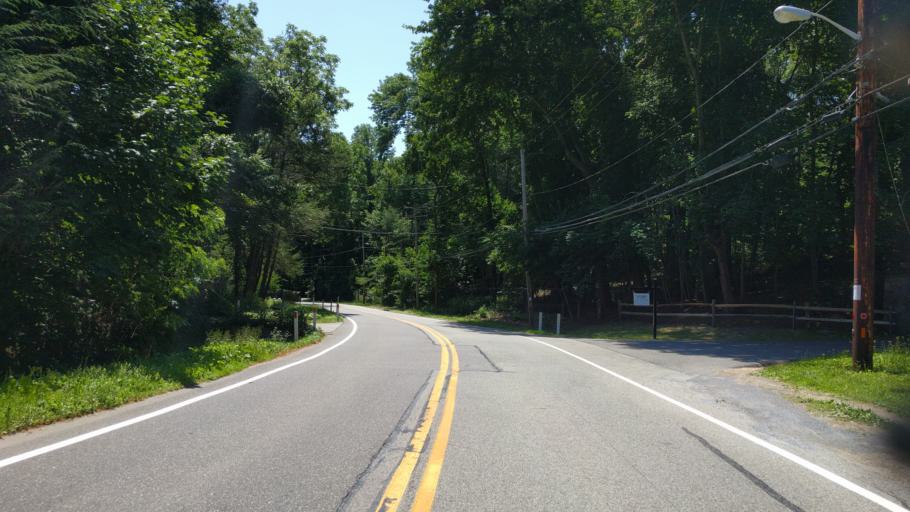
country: US
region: New York
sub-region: Nassau County
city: East Norwich
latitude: 40.8530
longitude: -73.5489
